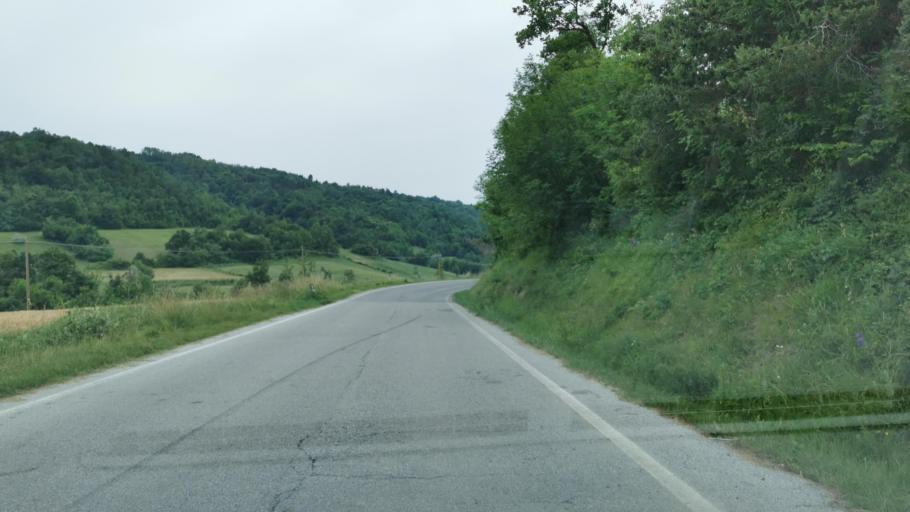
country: IT
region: Piedmont
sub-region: Provincia di Cuneo
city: Paroldo
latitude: 44.4266
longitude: 8.0577
